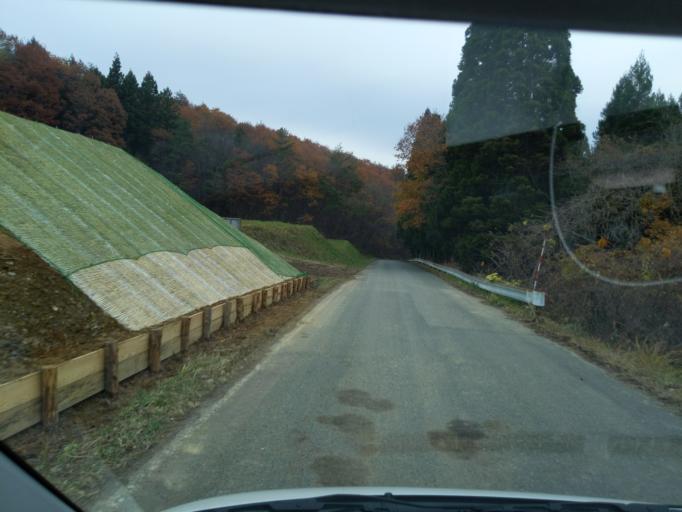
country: JP
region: Iwate
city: Ichinoseki
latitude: 39.0036
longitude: 141.0277
